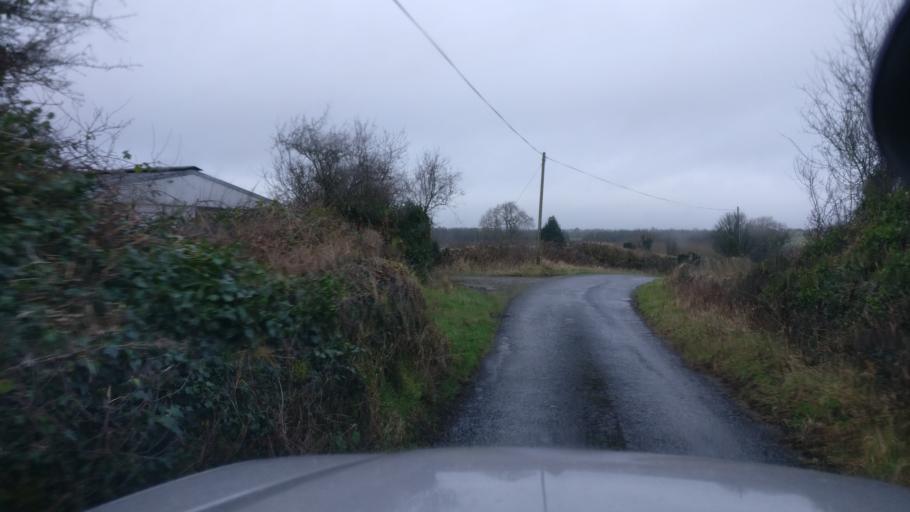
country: IE
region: Connaught
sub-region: County Galway
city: Loughrea
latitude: 53.1736
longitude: -8.6120
